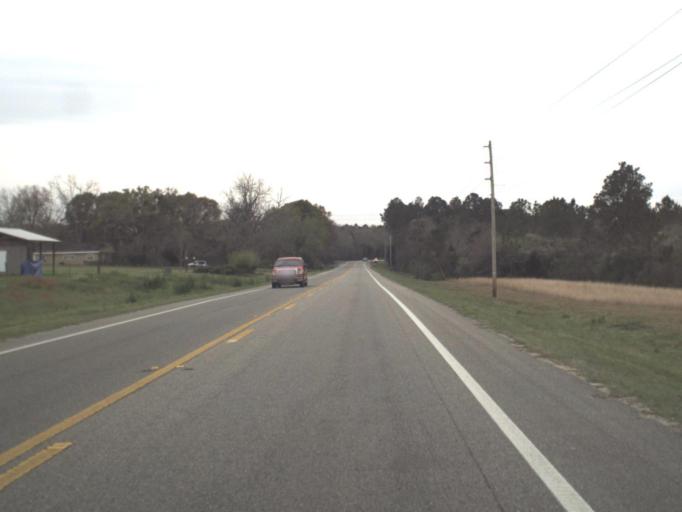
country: US
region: Florida
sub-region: Gulf County
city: Wewahitchka
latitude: 30.1519
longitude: -85.2094
